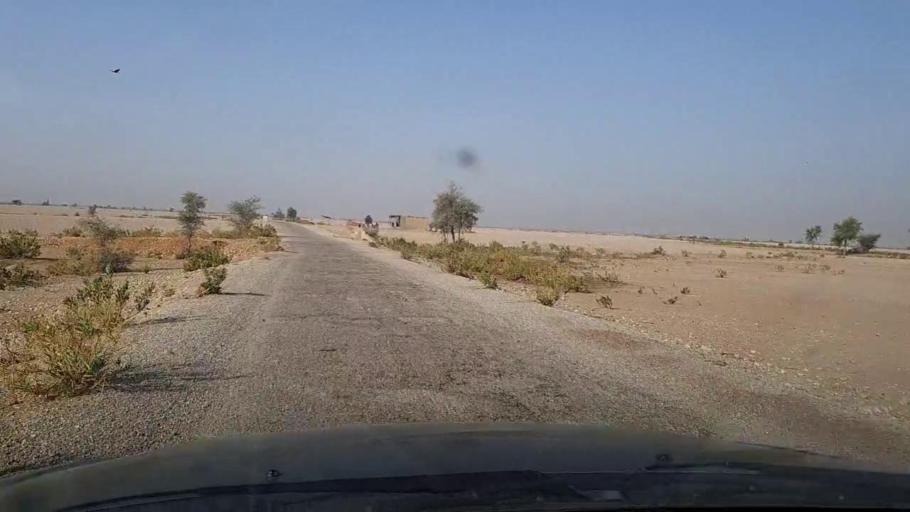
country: PK
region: Sindh
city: Sann
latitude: 25.9999
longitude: 68.0769
